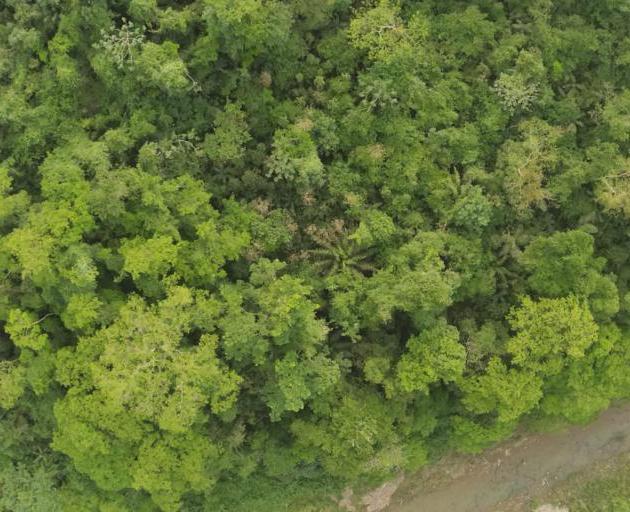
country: BO
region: La Paz
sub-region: Provincia Larecaja
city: Guanay
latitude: -15.7707
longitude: -67.6620
